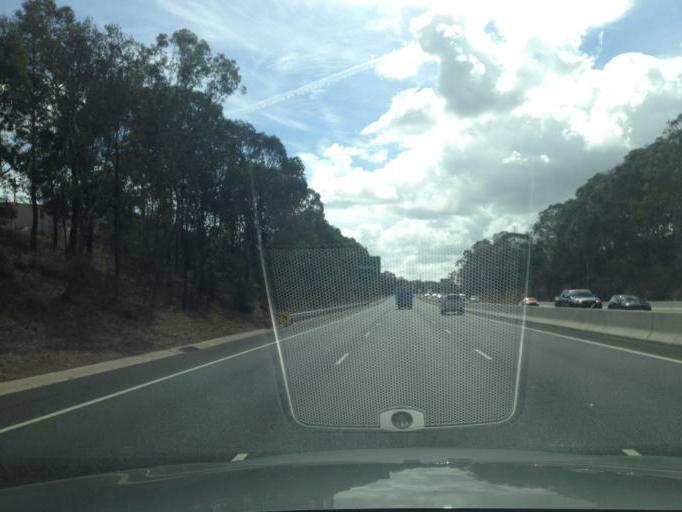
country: AU
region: New South Wales
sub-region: Bankstown
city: Revesby
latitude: -33.9425
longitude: 151.0008
